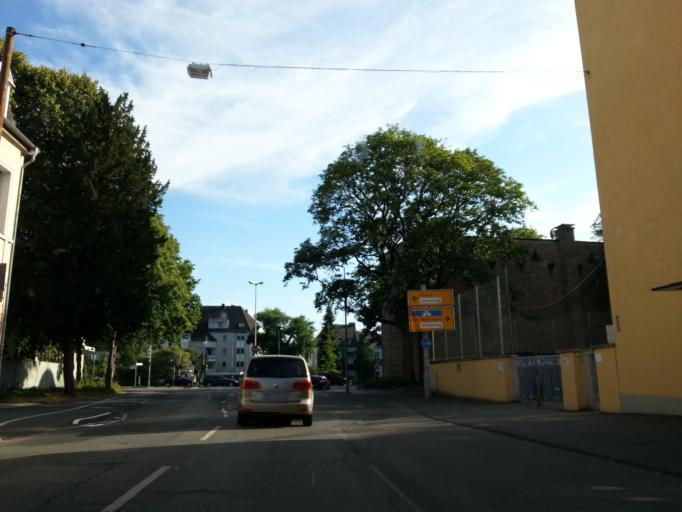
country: DE
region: Rheinland-Pfalz
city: Trier
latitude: 49.7511
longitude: 6.6351
